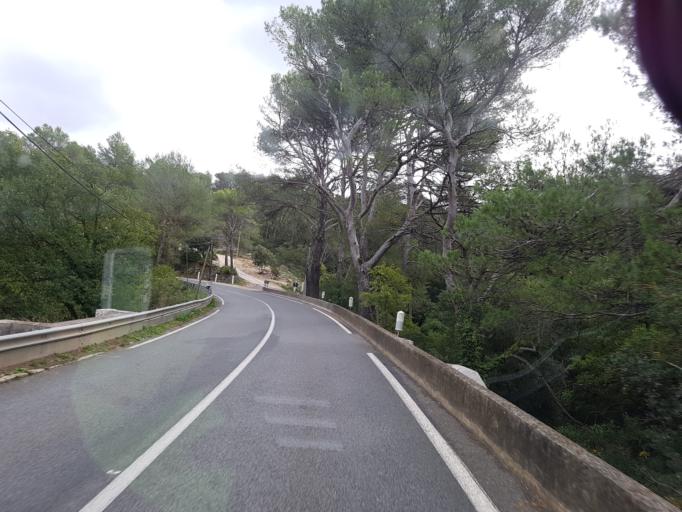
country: FR
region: Provence-Alpes-Cote d'Azur
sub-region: Departement des Bouches-du-Rhone
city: Cuges-les-Pins
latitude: 43.2665
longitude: 5.7286
